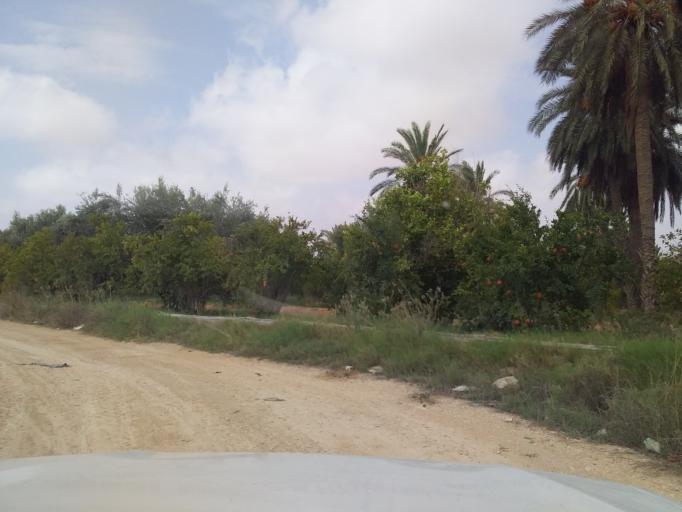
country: TN
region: Qabis
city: Gabes
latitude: 33.6265
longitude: 10.3088
